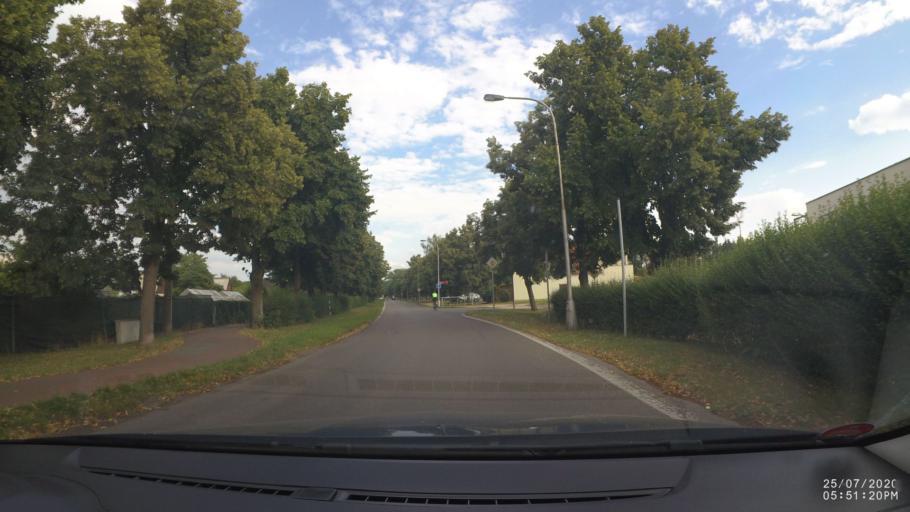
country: CZ
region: Kralovehradecky
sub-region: Okres Hradec Kralove
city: Hradec Kralove
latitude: 50.1964
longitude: 15.8634
